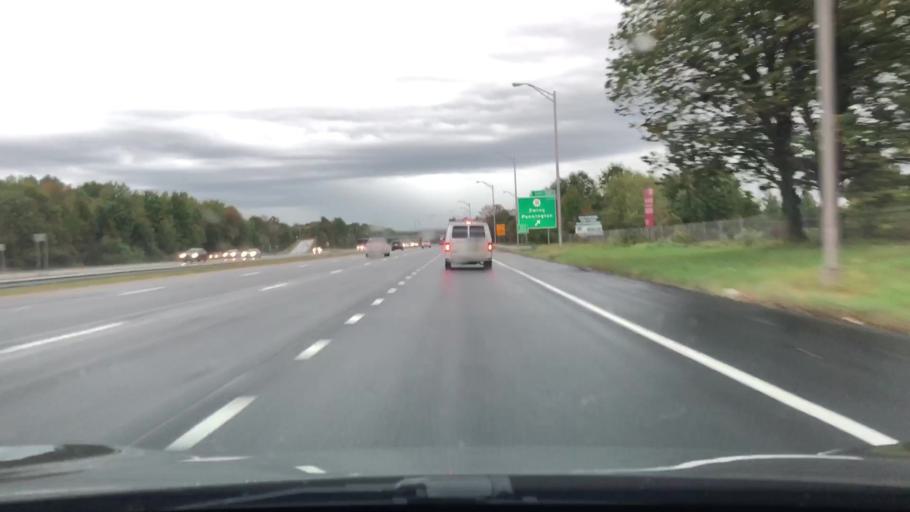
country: US
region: New Jersey
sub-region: Mercer County
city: Ewing
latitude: 40.2897
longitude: -74.7901
